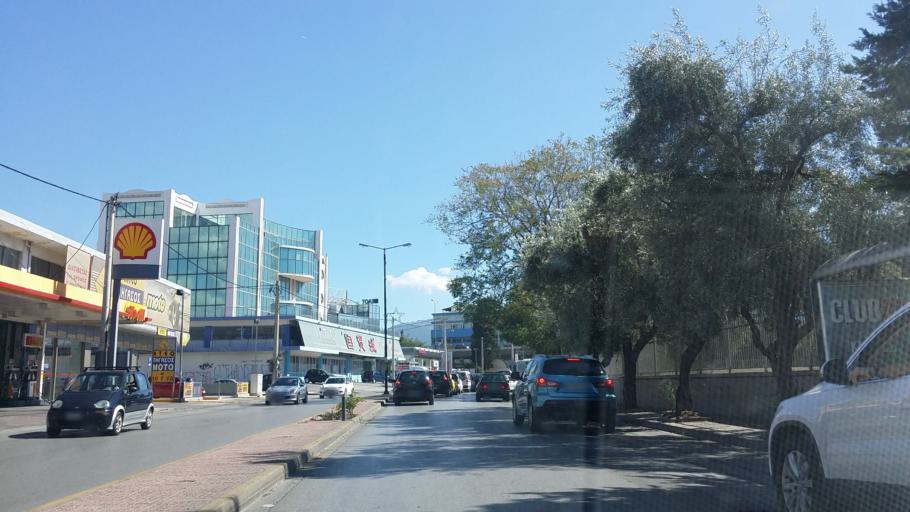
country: GR
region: Attica
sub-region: Nomarchia Athinas
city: Peristeri
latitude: 38.0097
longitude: 23.7130
